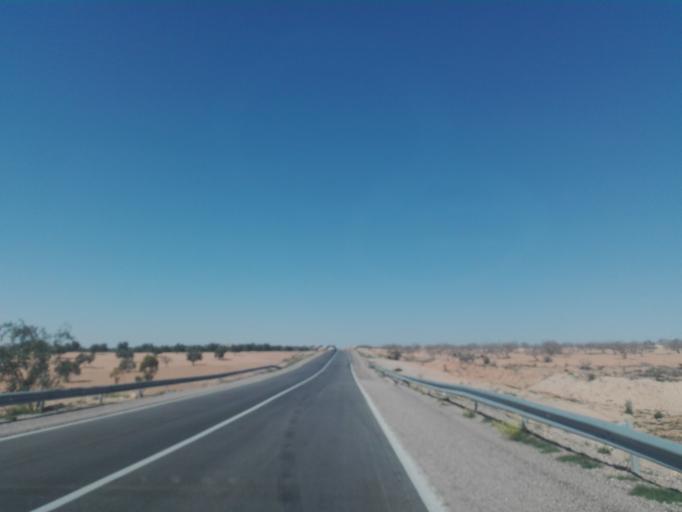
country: TN
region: Safaqis
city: Bi'r `Ali Bin Khalifah
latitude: 34.7584
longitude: 10.2916
